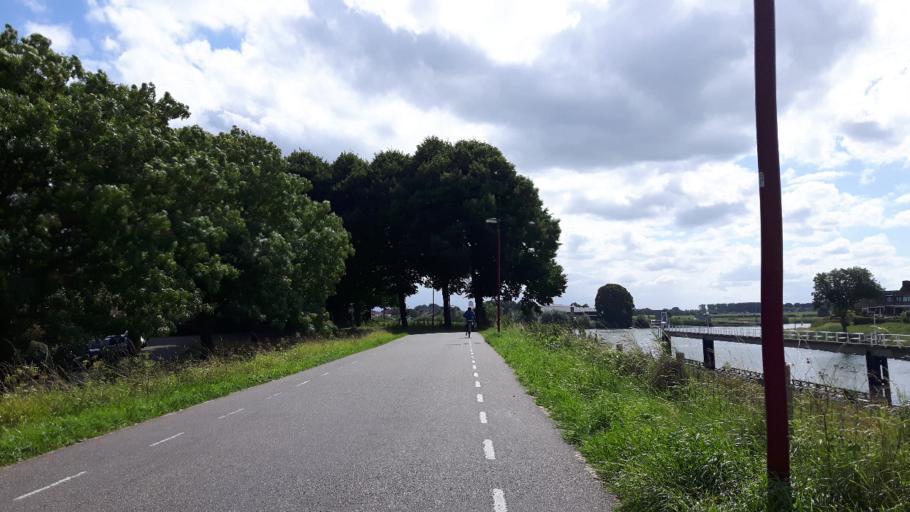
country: NL
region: Utrecht
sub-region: Gemeente Vianen
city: Vianen
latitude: 52.0046
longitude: 5.0931
